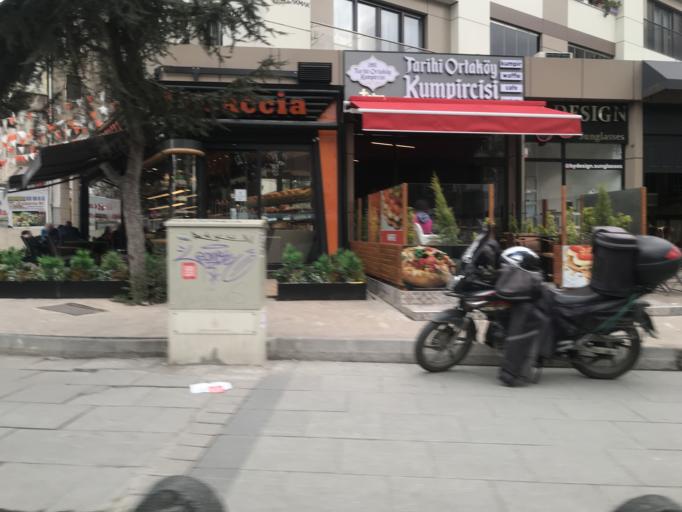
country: TR
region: Istanbul
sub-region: Atasehir
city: Atasehir
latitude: 40.9725
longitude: 29.0832
